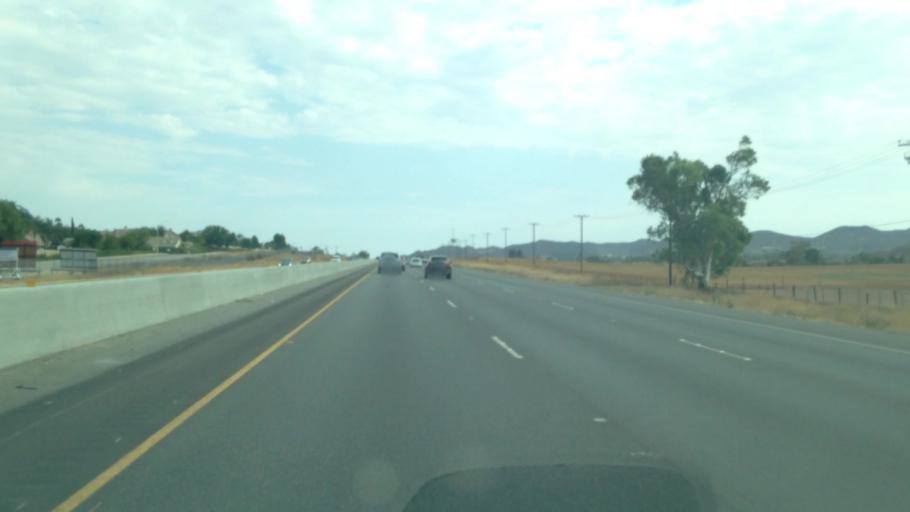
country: US
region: California
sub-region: Riverside County
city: Sun City
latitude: 33.6699
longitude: -117.1710
